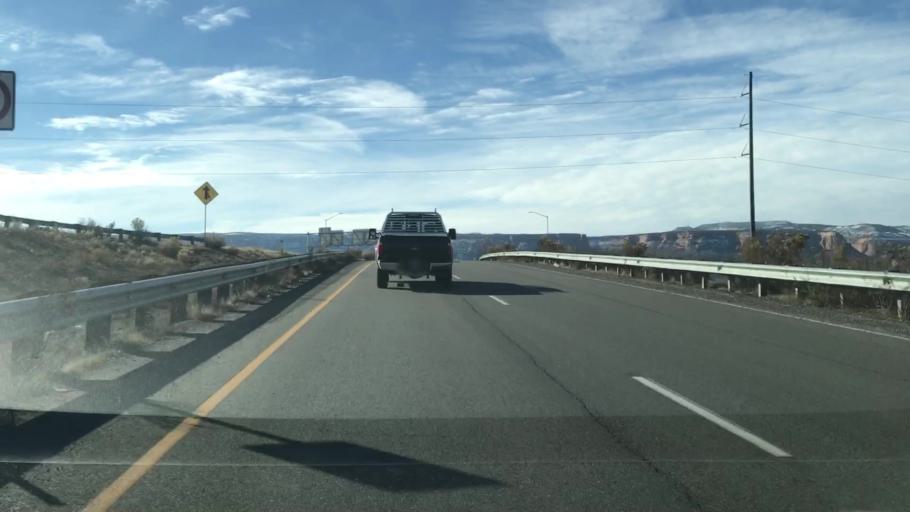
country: US
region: Colorado
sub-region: Mesa County
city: Redlands
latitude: 39.1122
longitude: -108.6458
